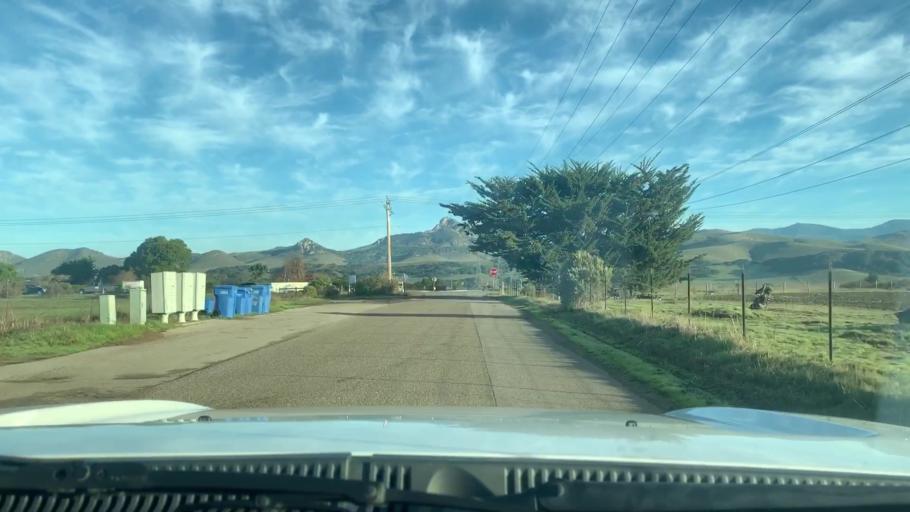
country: US
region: California
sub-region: San Luis Obispo County
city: Los Osos
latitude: 35.3024
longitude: -120.8010
